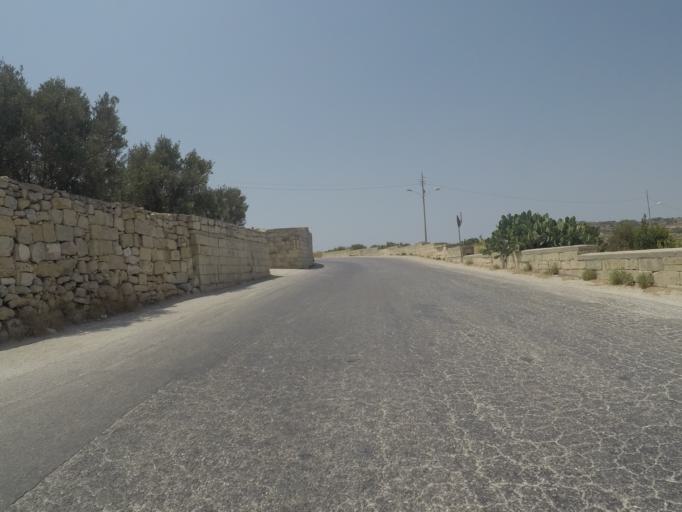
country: MT
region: Is-Siggiewi
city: Siggiewi
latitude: 35.8427
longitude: 14.4340
